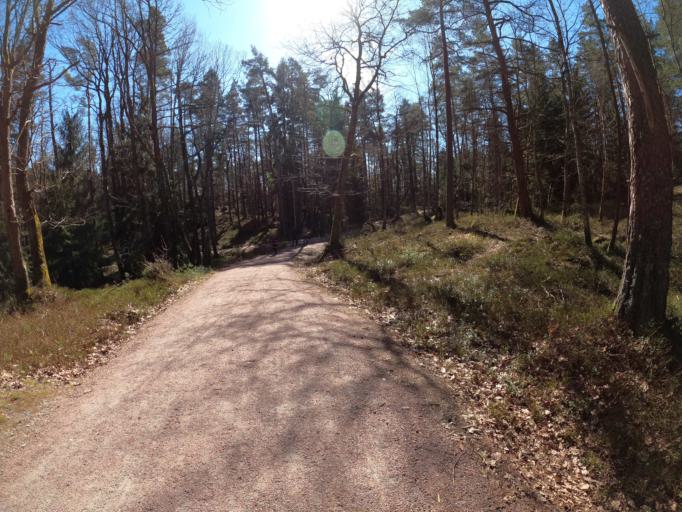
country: SE
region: Vaestra Goetaland
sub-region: Harryda Kommun
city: Molnlycke
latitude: 57.6382
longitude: 12.1288
